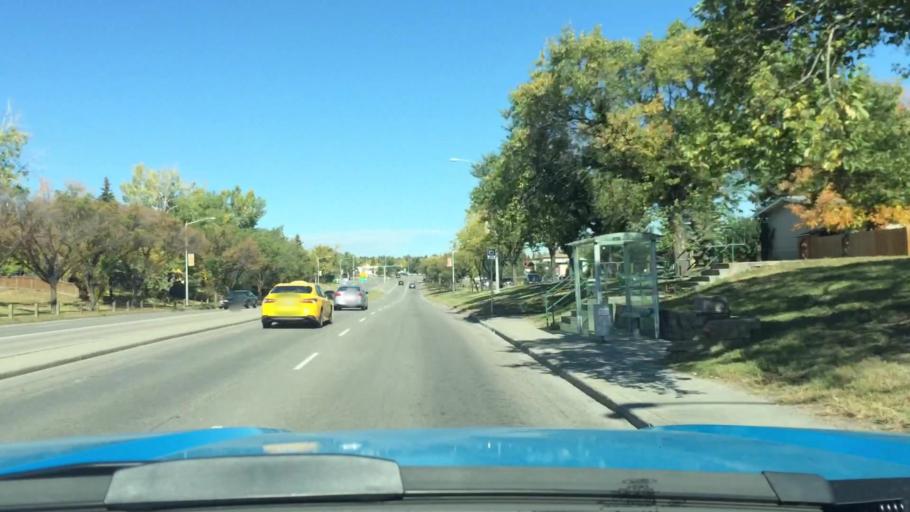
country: CA
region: Alberta
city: Calgary
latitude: 51.1136
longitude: -114.0647
